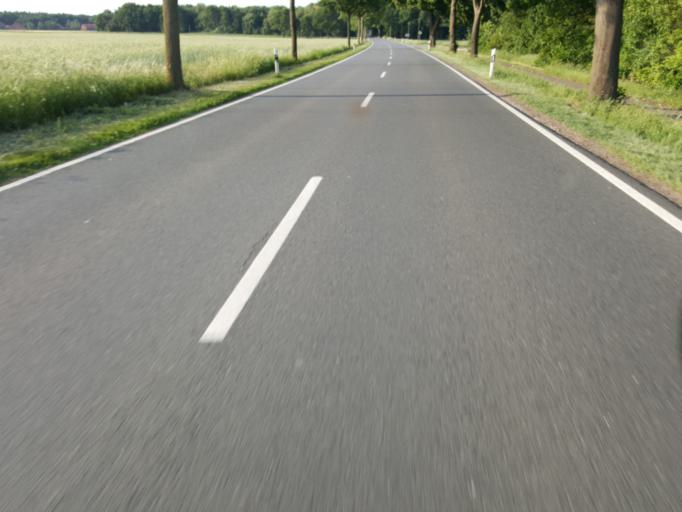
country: DE
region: Lower Saxony
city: Landesbergen
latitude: 52.5378
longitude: 9.1167
